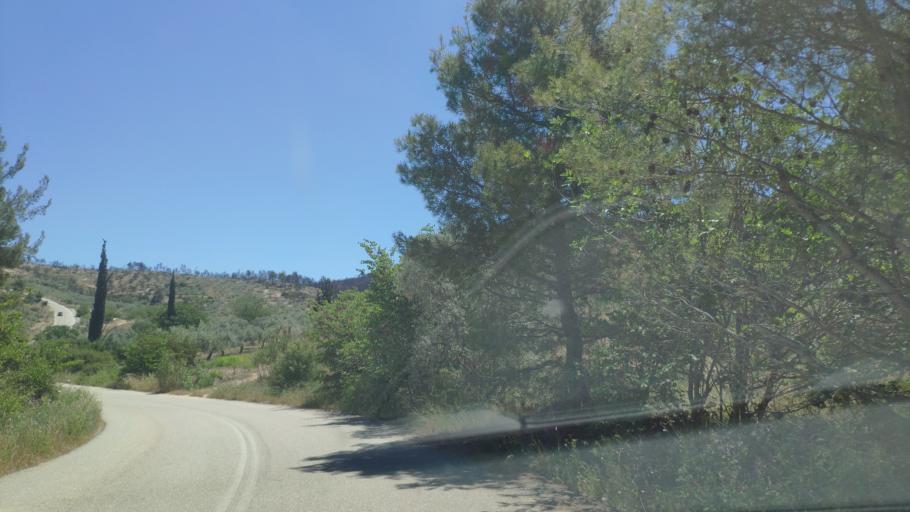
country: GR
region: Peloponnese
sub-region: Nomos Korinthias
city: Athikia
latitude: 37.8351
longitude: 22.9338
